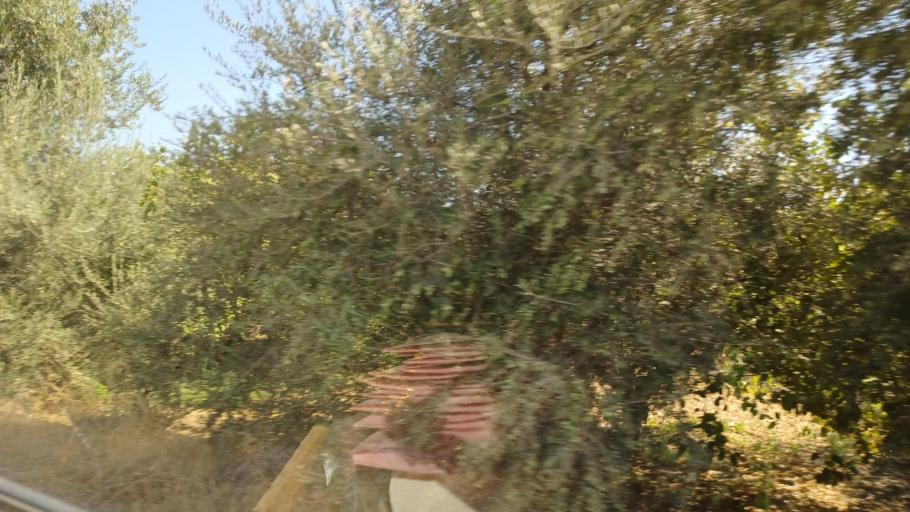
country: CY
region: Pafos
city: Polis
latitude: 35.0461
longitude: 32.4575
